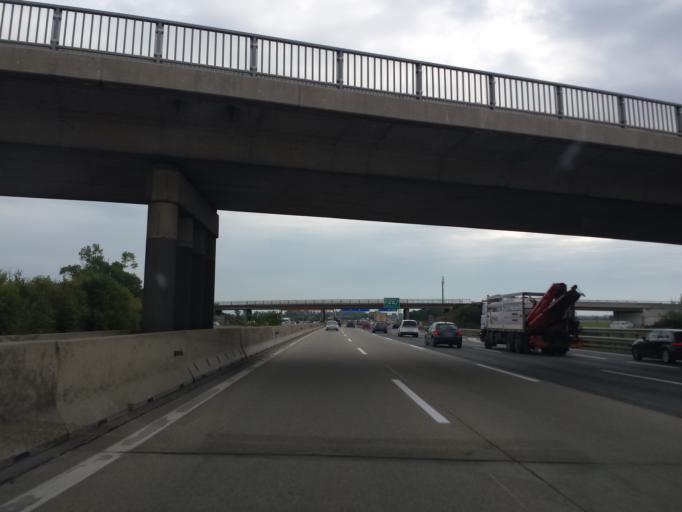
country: AT
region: Lower Austria
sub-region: Politischer Bezirk Modling
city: Guntramsdorf
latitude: 48.0396
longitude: 16.3411
